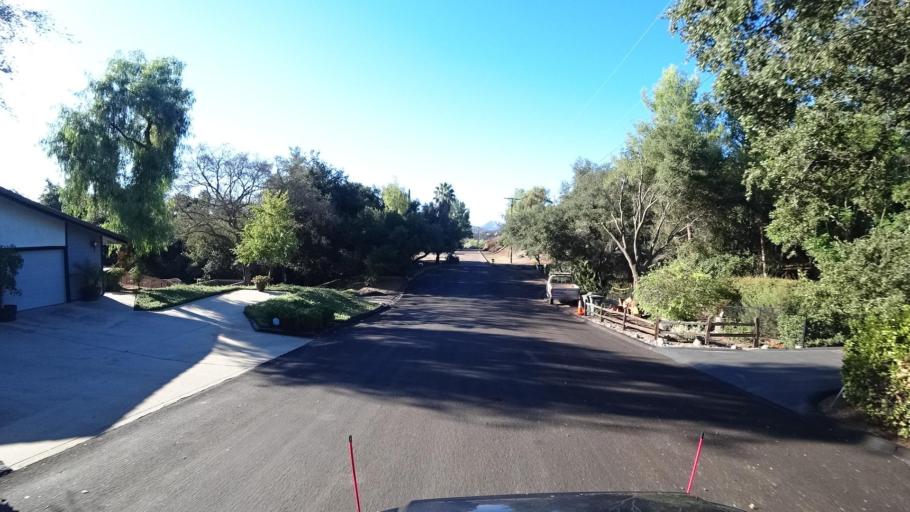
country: US
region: California
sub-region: San Diego County
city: Alpine
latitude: 32.8254
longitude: -116.7531
